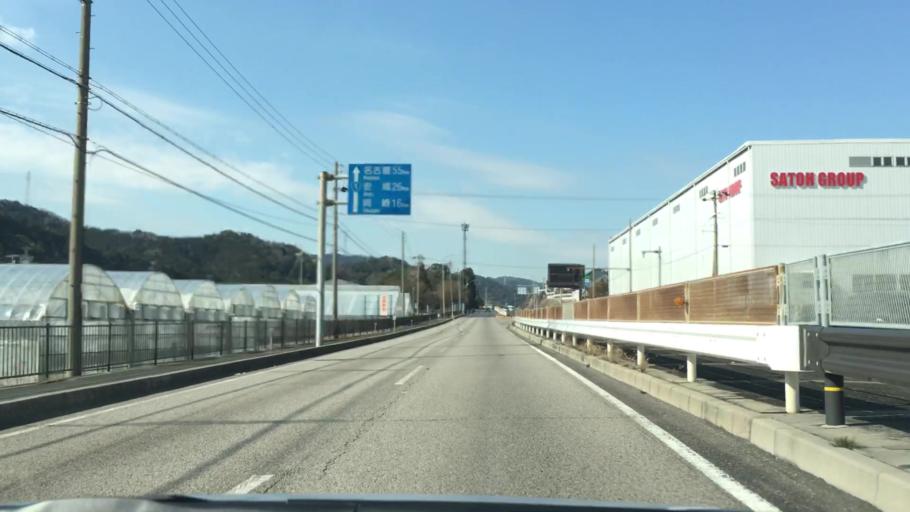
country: JP
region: Aichi
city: Gamagori
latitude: 34.8677
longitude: 137.2938
